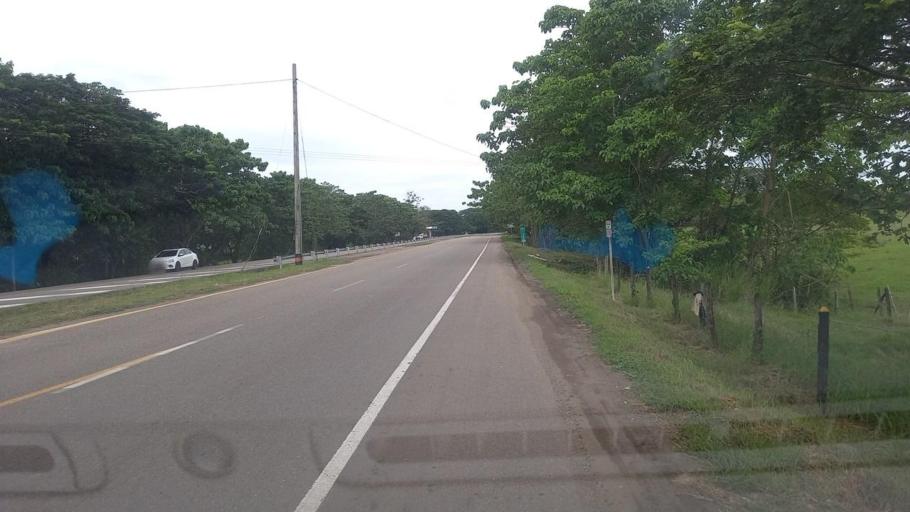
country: CO
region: Boyaca
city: Puerto Boyaca
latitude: 6.2191
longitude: -74.5516
